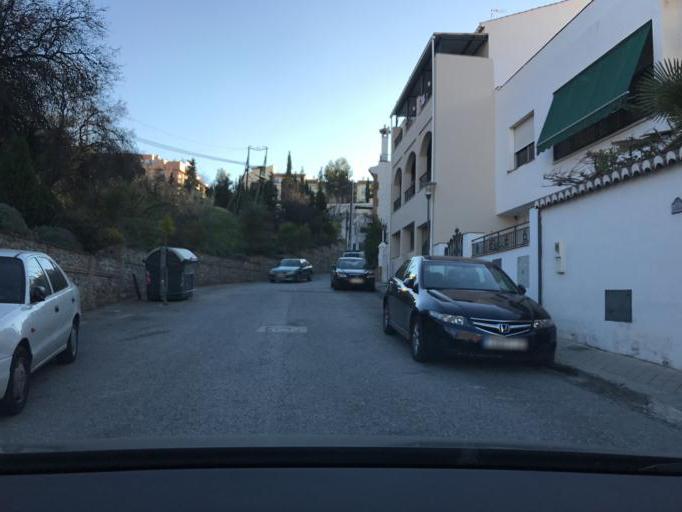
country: ES
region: Andalusia
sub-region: Provincia de Granada
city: Huetor Vega
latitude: 37.1629
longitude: -3.5830
